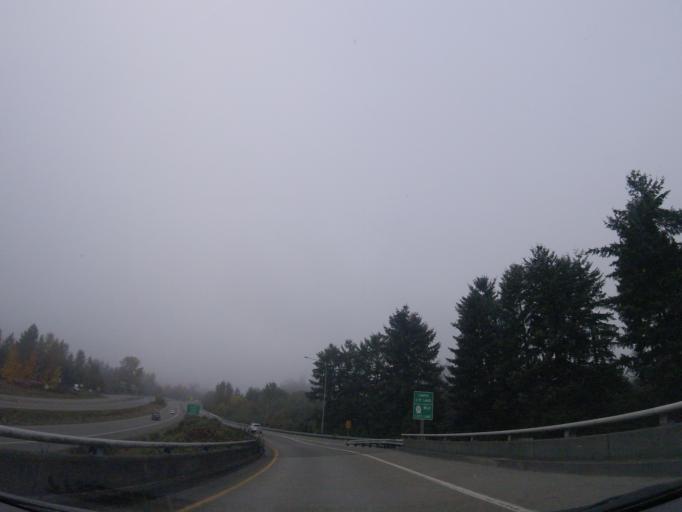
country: US
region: Washington
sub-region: King County
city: Bothell
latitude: 47.7590
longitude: -122.1861
